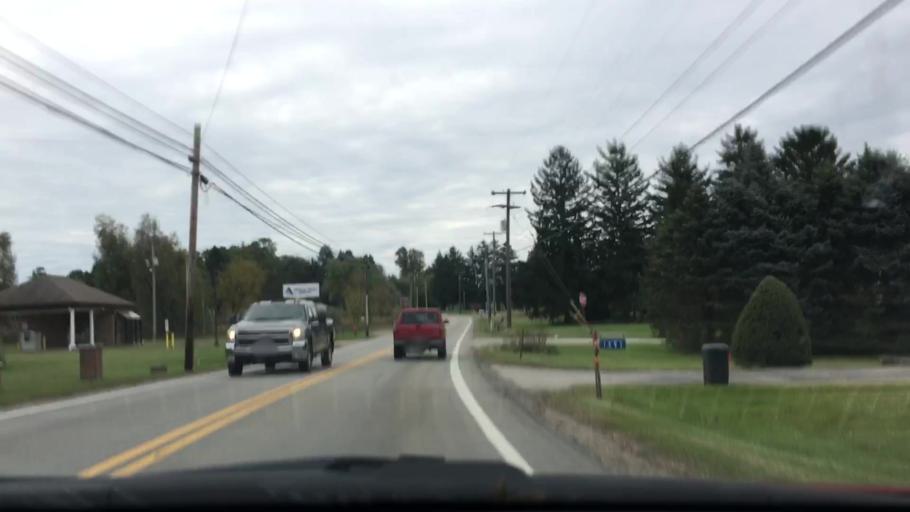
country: US
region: Pennsylvania
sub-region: Armstrong County
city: Orchard Hills
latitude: 40.6071
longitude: -79.4869
